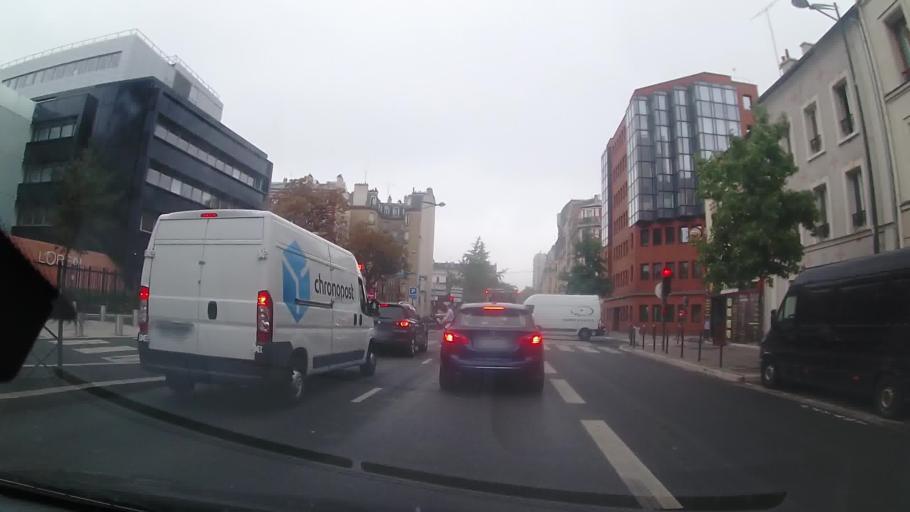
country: FR
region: Ile-de-France
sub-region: Departement des Hauts-de-Seine
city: Clichy
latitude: 48.9005
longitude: 2.3084
